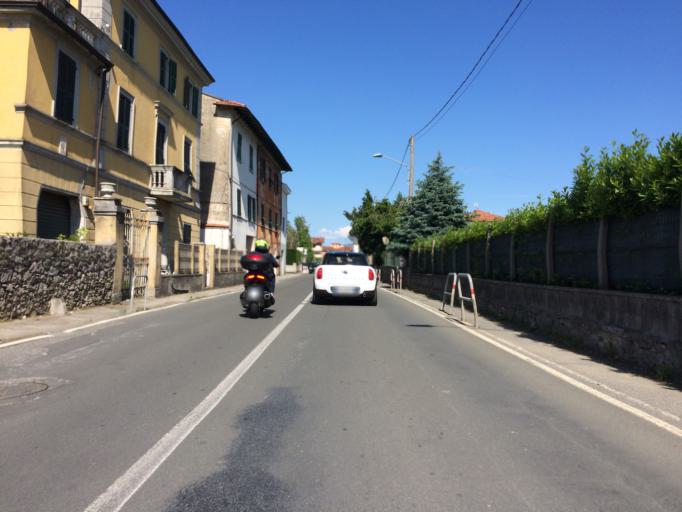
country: IT
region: Liguria
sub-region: Provincia di La Spezia
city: Sarzana
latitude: 44.1065
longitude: 9.9720
